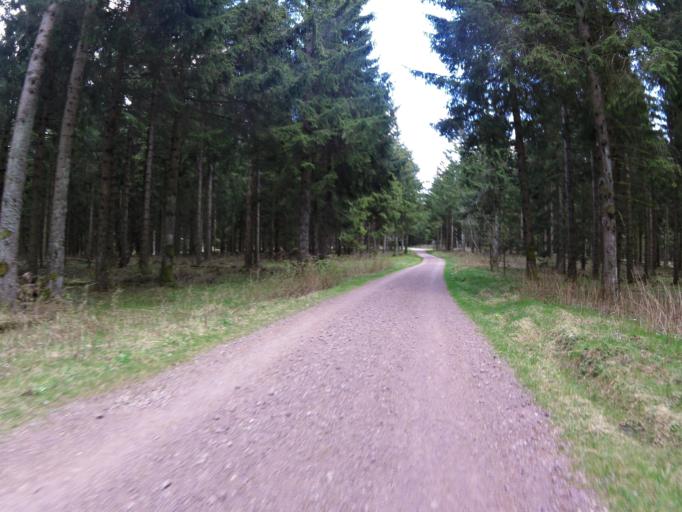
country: DE
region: Thuringia
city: Oberhof
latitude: 50.7078
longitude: 10.6811
